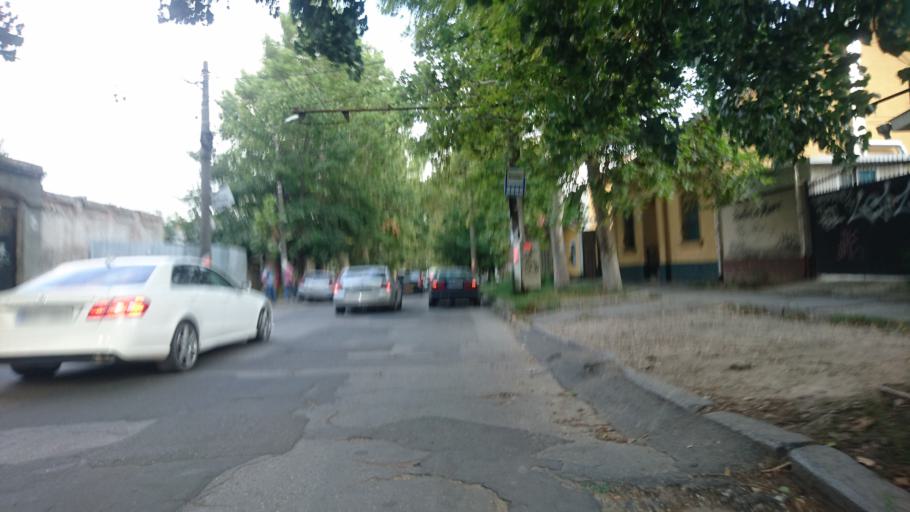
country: MD
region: Chisinau
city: Chisinau
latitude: 47.0151
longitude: 28.8406
